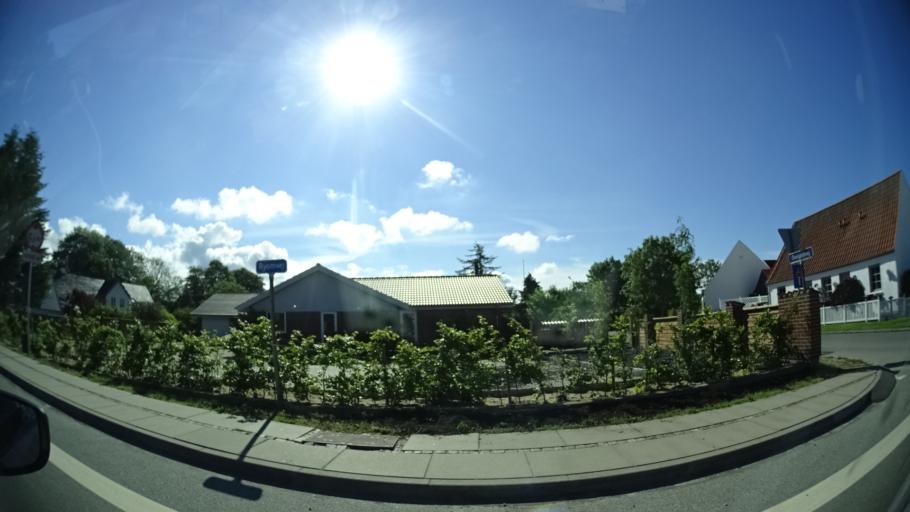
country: DK
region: Central Jutland
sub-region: Syddjurs Kommune
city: Ronde
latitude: 56.3076
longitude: 10.4156
